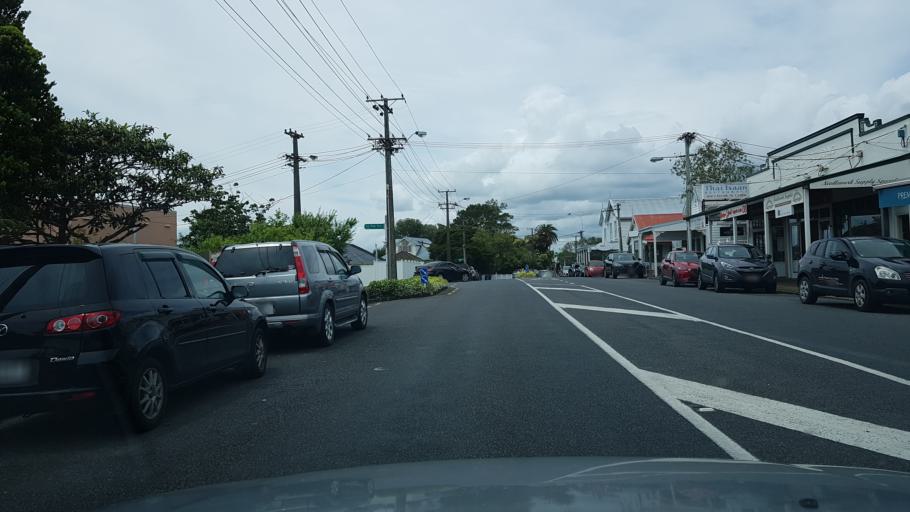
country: NZ
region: Auckland
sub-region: Auckland
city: North Shore
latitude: -36.8152
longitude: 174.7307
